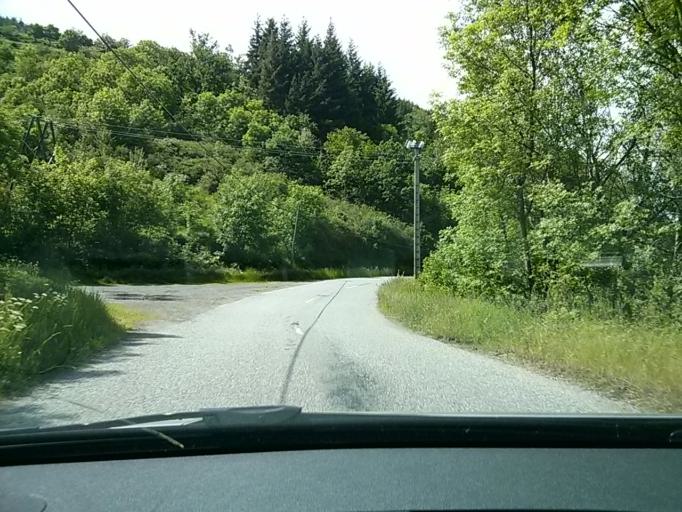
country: FR
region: Rhone-Alpes
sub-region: Departement de la Loire
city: Saint-Chamond
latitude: 45.4177
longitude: 4.5306
